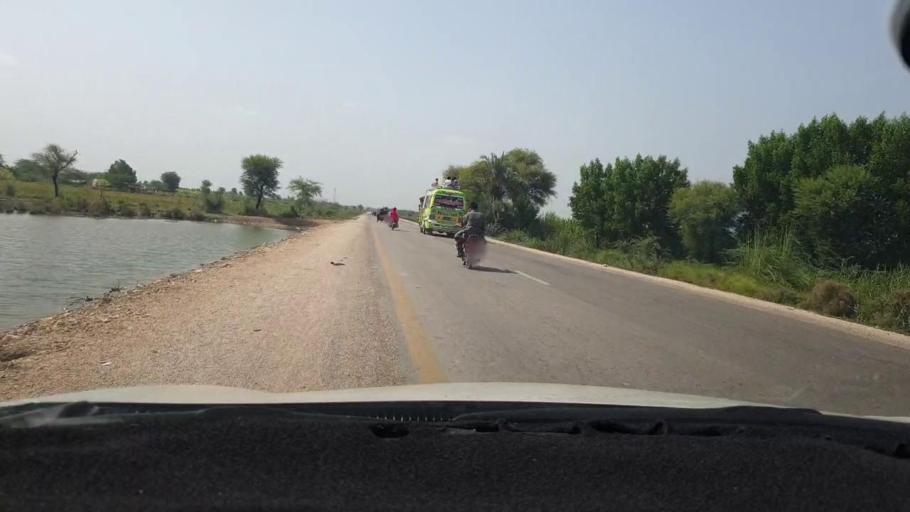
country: PK
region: Sindh
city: Mirpur Khas
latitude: 25.5849
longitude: 69.0743
